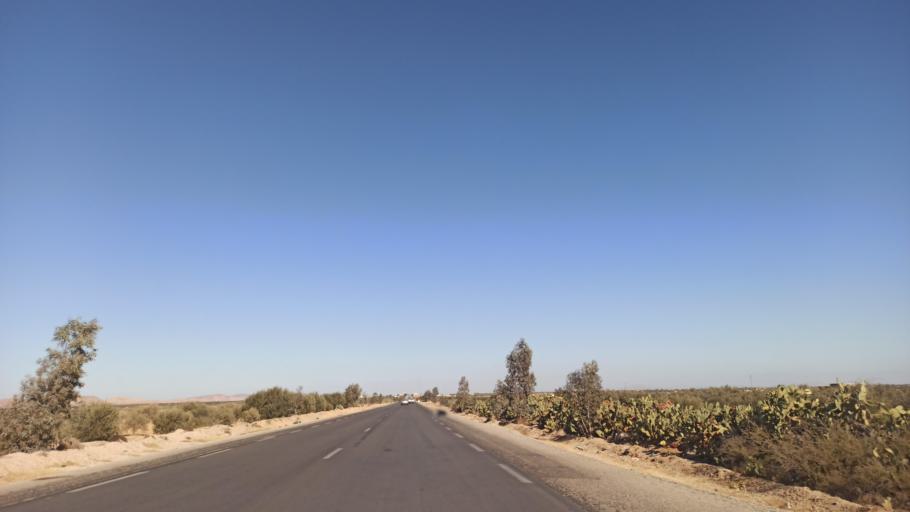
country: TN
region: Sidi Bu Zayd
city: Bi'r al Hufayy
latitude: 34.9546
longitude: 9.2154
